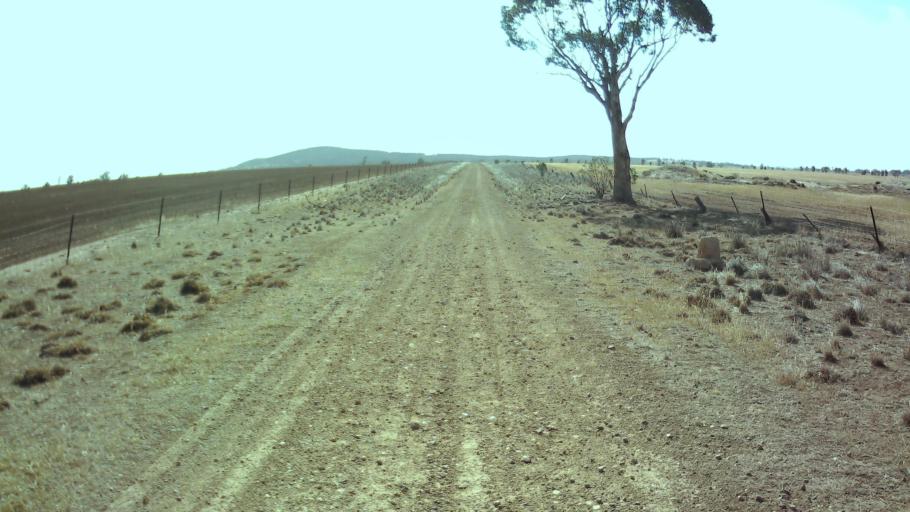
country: AU
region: New South Wales
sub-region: Weddin
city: Grenfell
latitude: -33.7325
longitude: 147.9980
